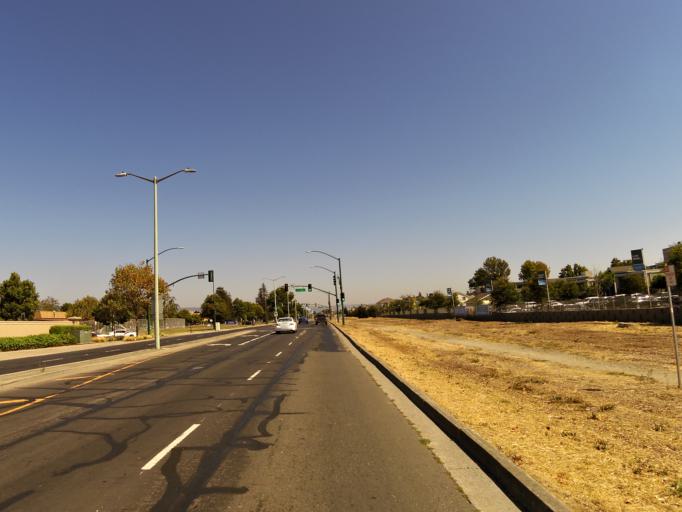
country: US
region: California
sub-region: Alameda County
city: Oakland
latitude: 37.7798
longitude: -122.2832
